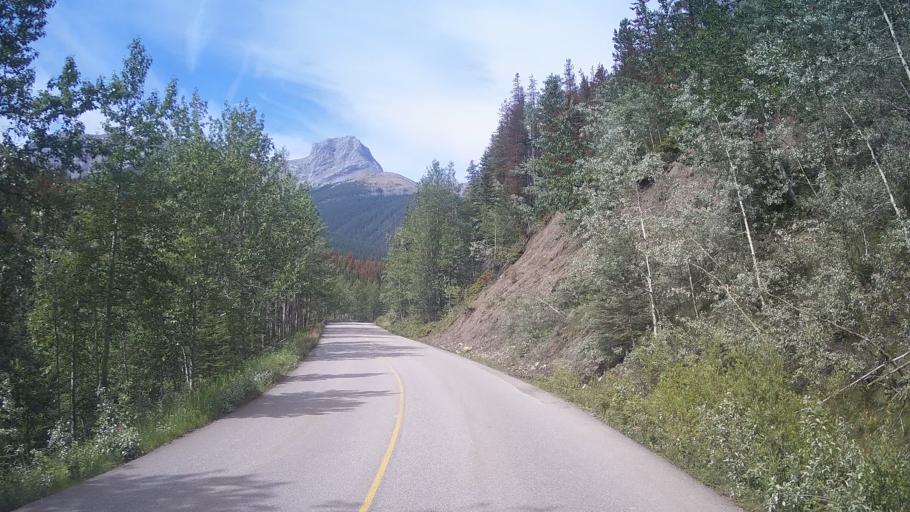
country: CA
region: Alberta
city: Hinton
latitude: 53.1774
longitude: -117.8479
